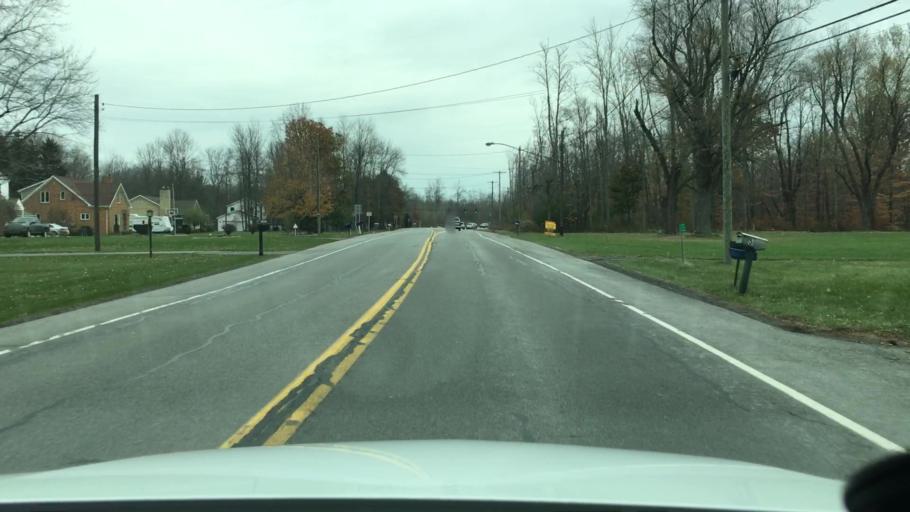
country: US
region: New York
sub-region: Erie County
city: Lancaster
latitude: 42.8588
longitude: -78.6795
